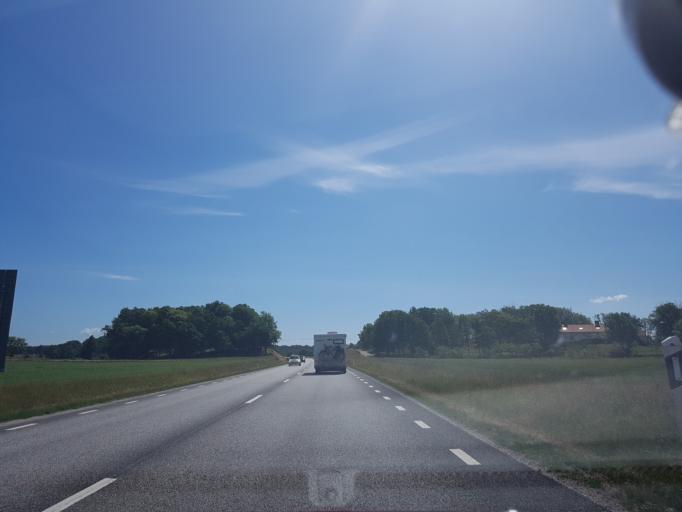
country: SE
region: Vaestra Goetaland
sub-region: Orust
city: Henan
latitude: 58.1480
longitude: 11.5945
